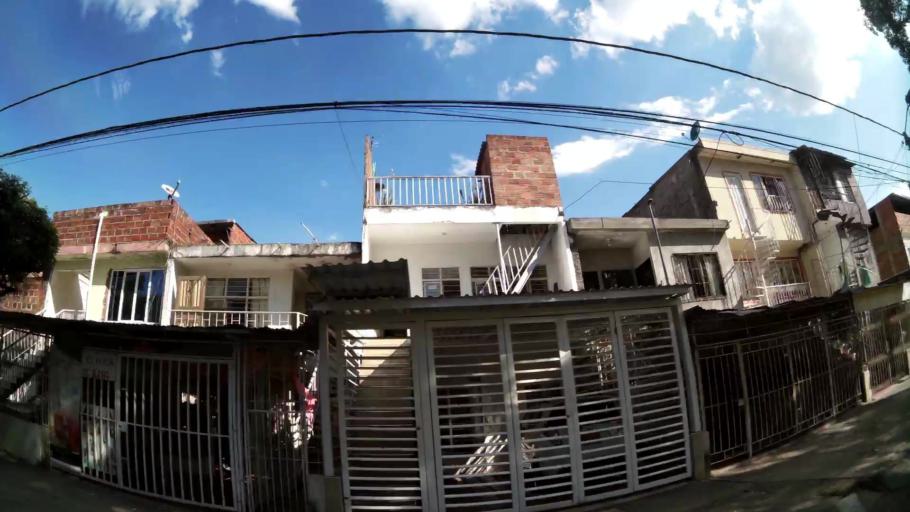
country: CO
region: Valle del Cauca
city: Cali
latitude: 3.4199
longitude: -76.5002
